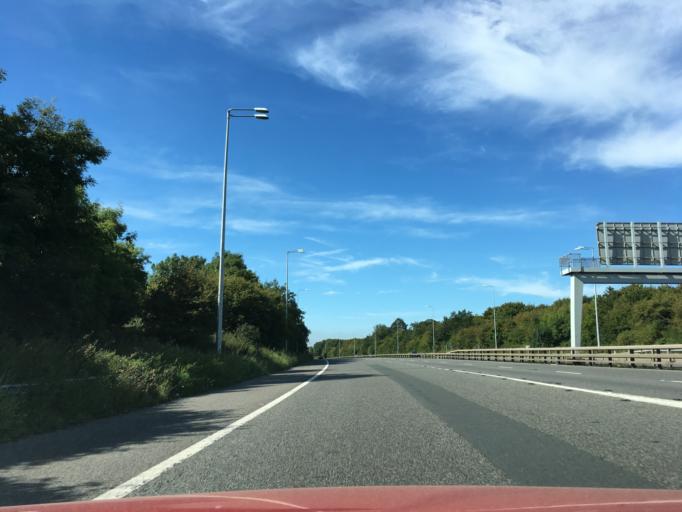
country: GB
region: England
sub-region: South Gloucestershire
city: Almondsbury
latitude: 51.5560
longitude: -2.5563
